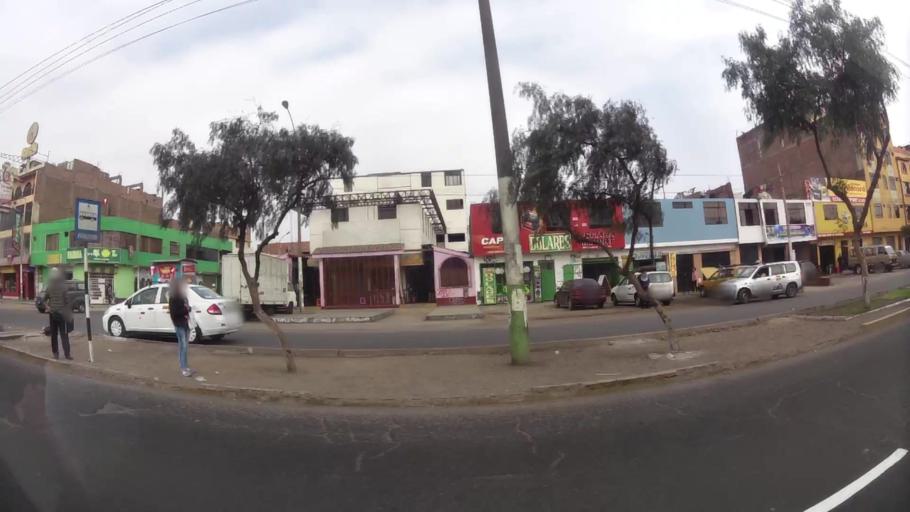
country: PE
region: Callao
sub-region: Callao
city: Callao
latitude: -12.0123
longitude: -77.0924
